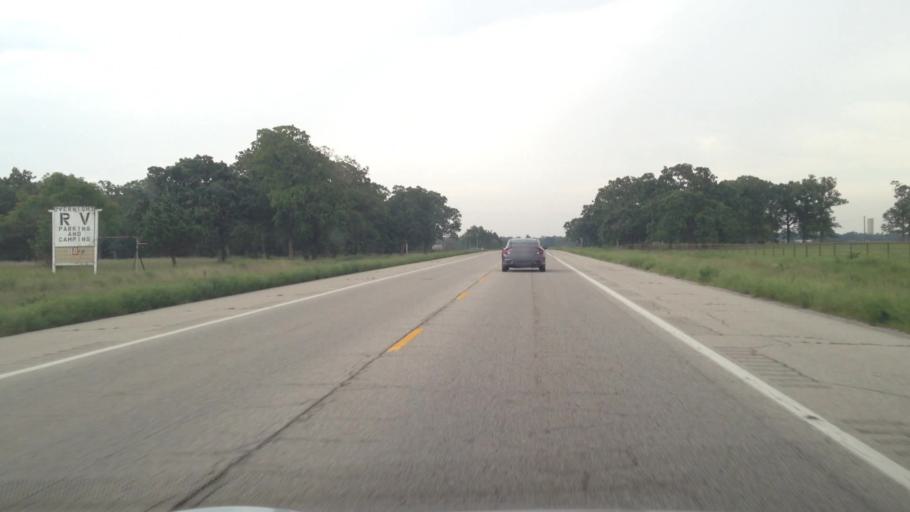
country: US
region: Kansas
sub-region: Cherokee County
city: Galena
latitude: 37.0153
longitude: -94.6330
